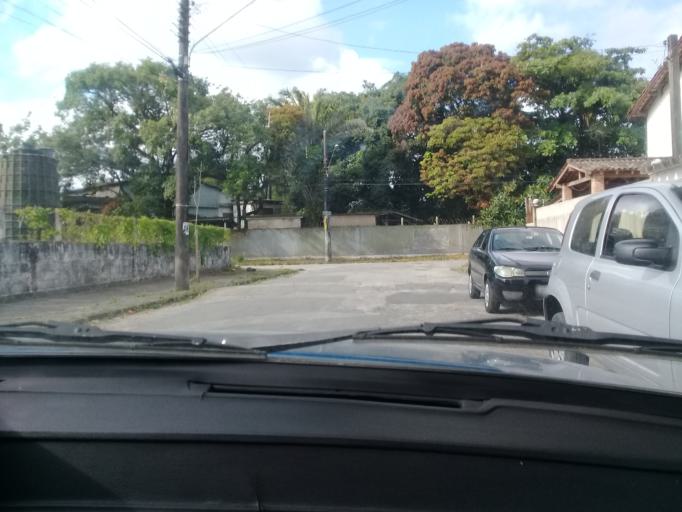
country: BR
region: Sao Paulo
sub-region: Guaruja
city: Guaruja
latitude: -23.9876
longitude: -46.2792
